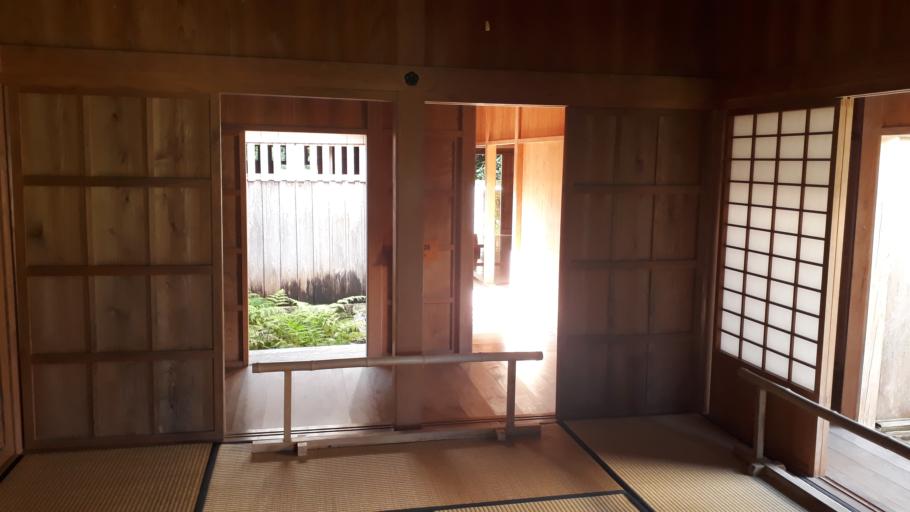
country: JP
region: Okinawa
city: Naha-shi
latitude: 26.2031
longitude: 127.7167
